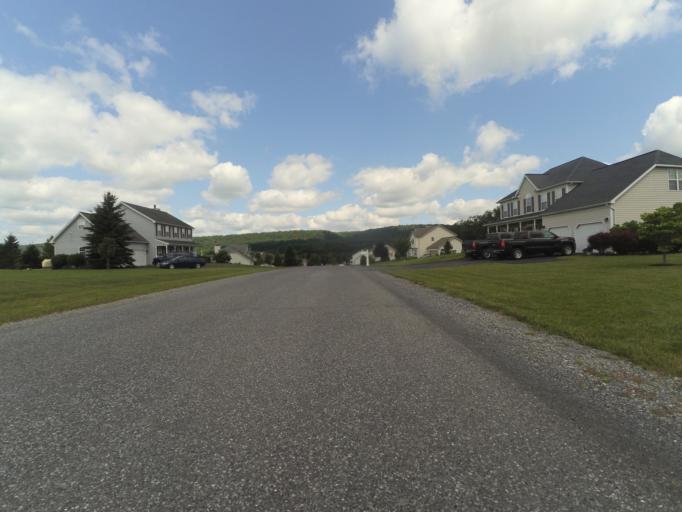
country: US
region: Pennsylvania
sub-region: Centre County
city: Stormstown
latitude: 40.7997
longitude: -77.9975
